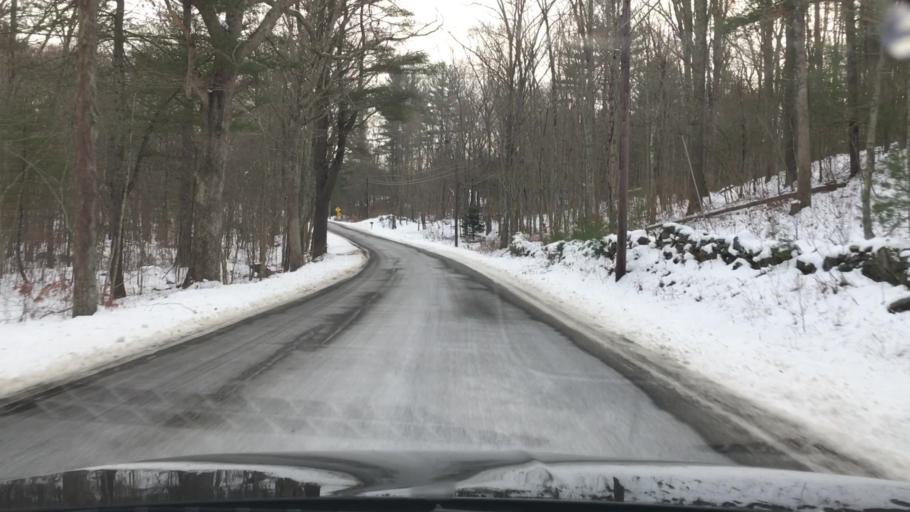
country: US
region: Connecticut
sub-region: Tolland County
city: Storrs
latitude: 41.8504
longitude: -72.1819
